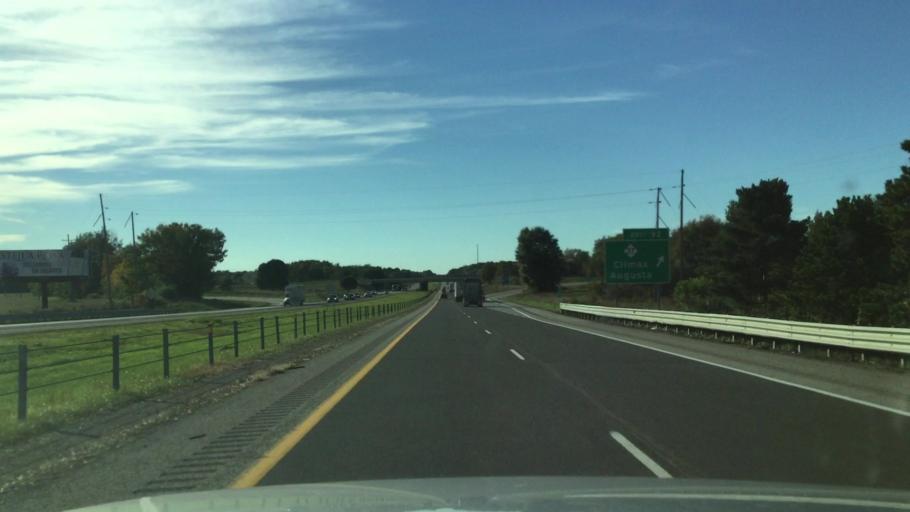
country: US
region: Michigan
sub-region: Calhoun County
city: Springfield
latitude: 42.2714
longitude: -85.2887
